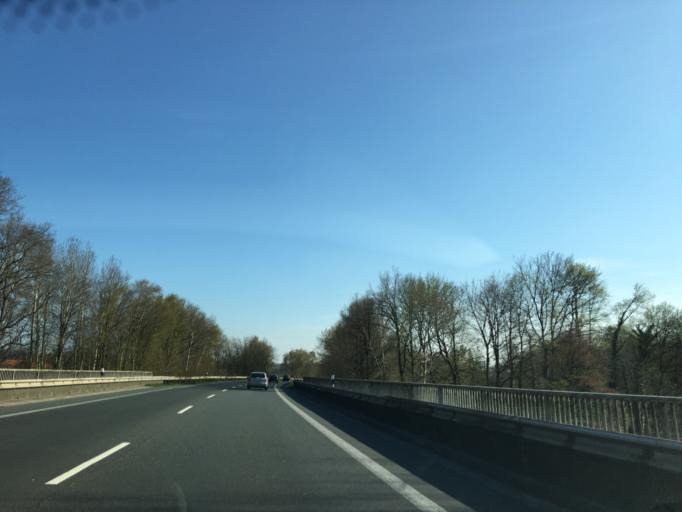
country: DE
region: North Rhine-Westphalia
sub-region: Regierungsbezirk Munster
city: Muenster
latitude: 52.0437
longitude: 7.6851
